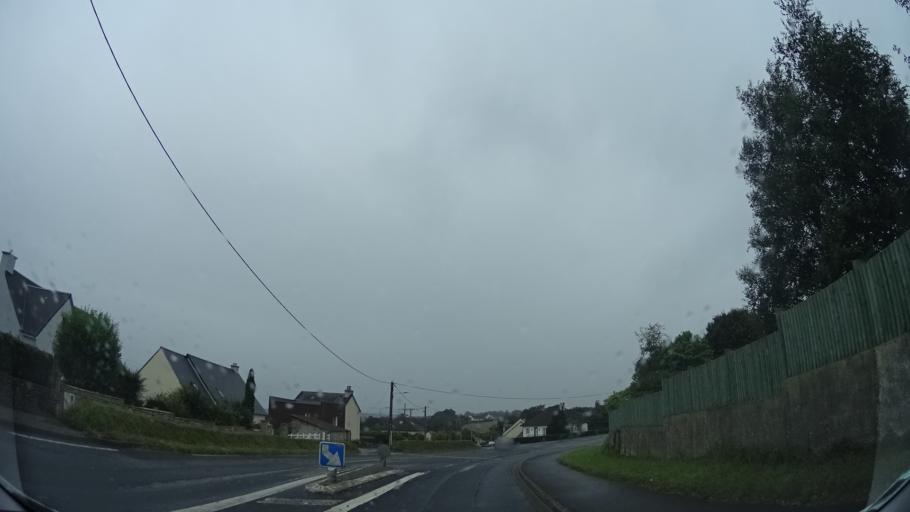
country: FR
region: Lower Normandy
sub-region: Departement de la Manche
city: Octeville
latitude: 49.6203
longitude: -1.6578
